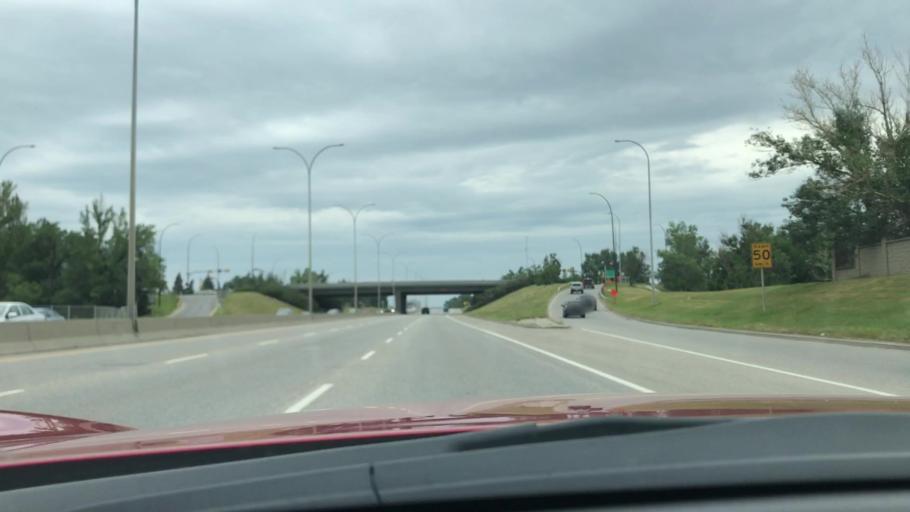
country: CA
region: Alberta
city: Calgary
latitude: 51.0219
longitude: -114.1178
